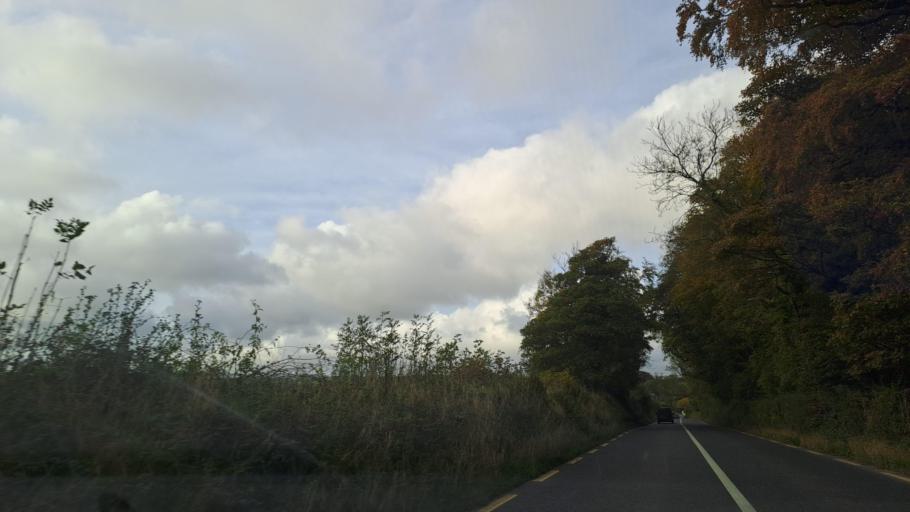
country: IE
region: Ulster
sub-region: An Cabhan
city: Kingscourt
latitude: 53.8552
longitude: -6.7810
